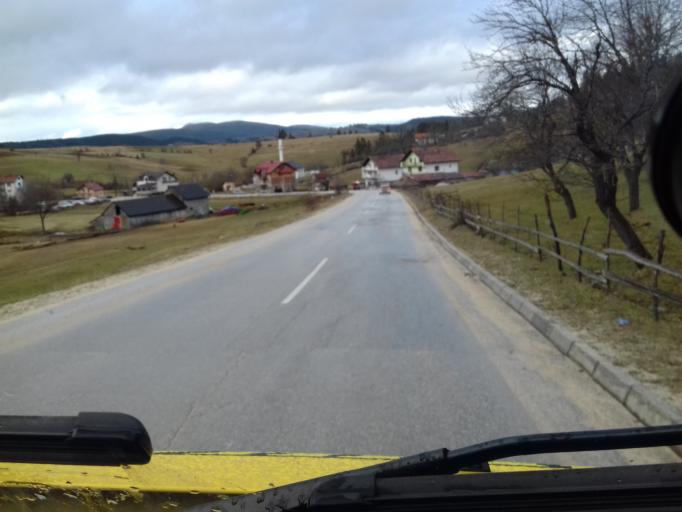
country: BA
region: Federation of Bosnia and Herzegovina
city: Turbe
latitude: 44.3141
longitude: 17.5296
